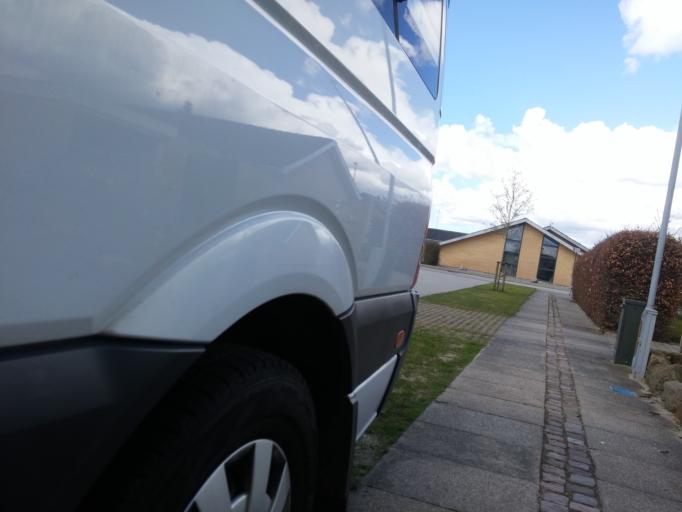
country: DK
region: Central Jutland
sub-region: Ringkobing-Skjern Kommune
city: Skjern
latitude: 55.9475
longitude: 8.5144
